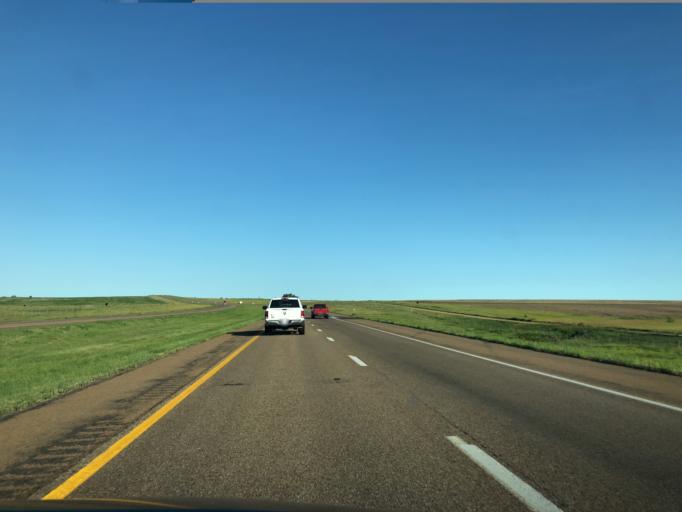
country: US
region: Kansas
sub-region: Ellis County
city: Ellis
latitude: 38.9781
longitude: -99.6883
